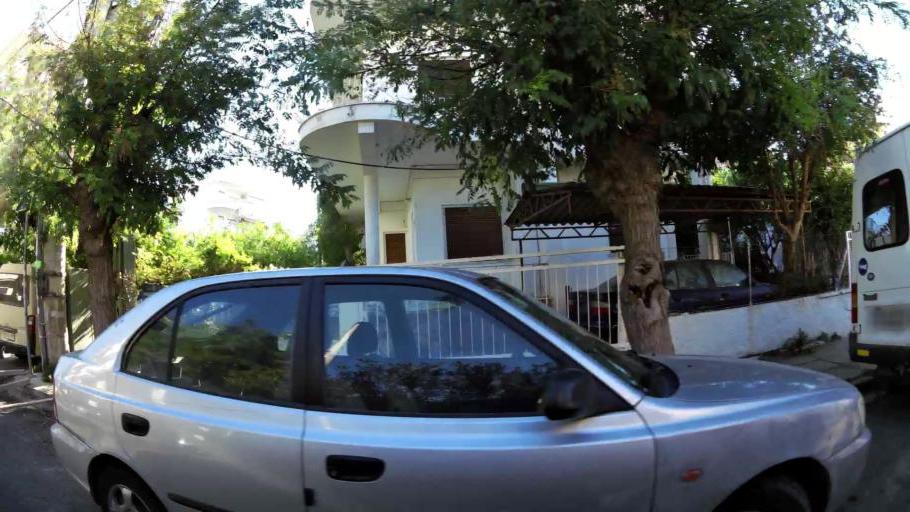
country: GR
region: Attica
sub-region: Nomarchia Athinas
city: Khalandrion
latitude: 38.0169
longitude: 23.7929
